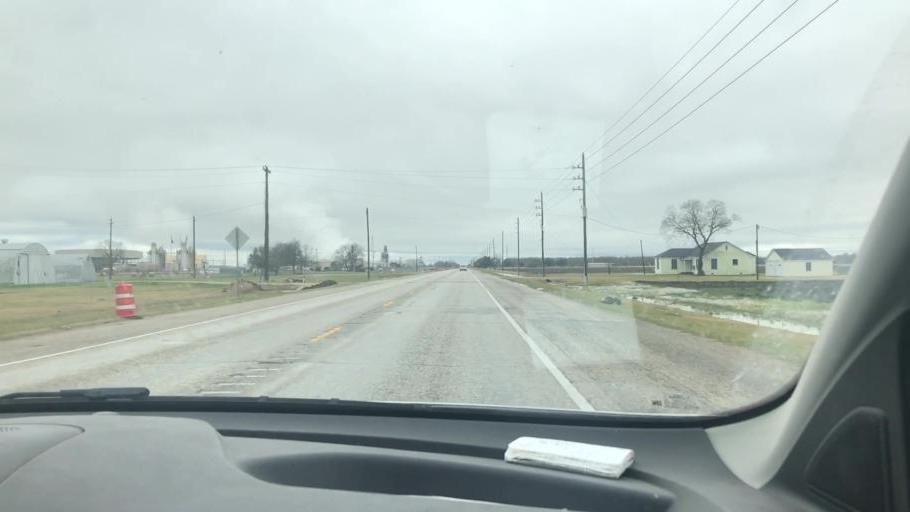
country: US
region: Texas
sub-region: Wharton County
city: Wharton
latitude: 29.2982
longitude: -96.0769
